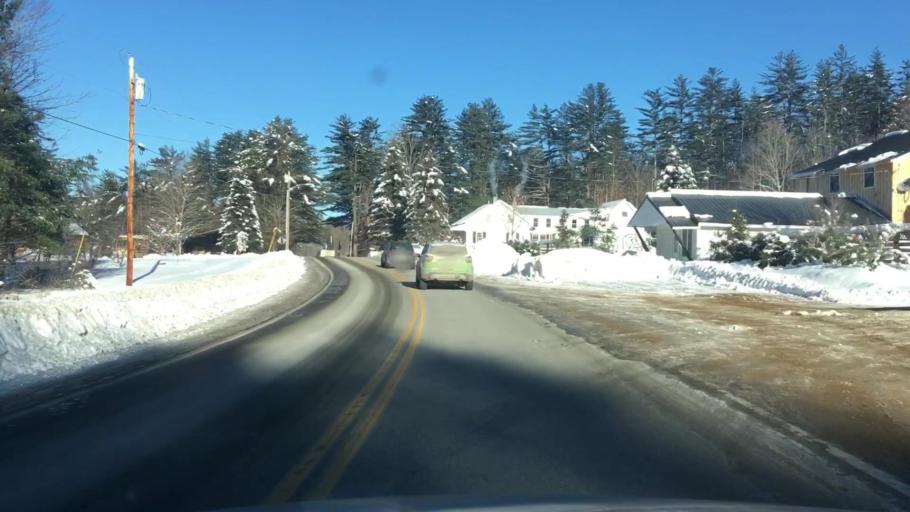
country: US
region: Maine
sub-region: Oxford County
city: West Paris
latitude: 44.4054
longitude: -70.6351
